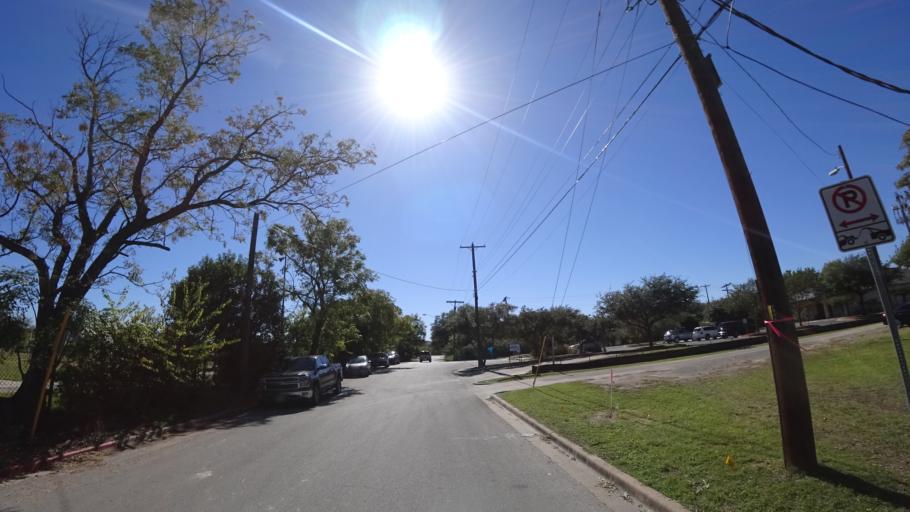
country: US
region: Texas
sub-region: Travis County
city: Austin
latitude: 30.3182
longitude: -97.7372
